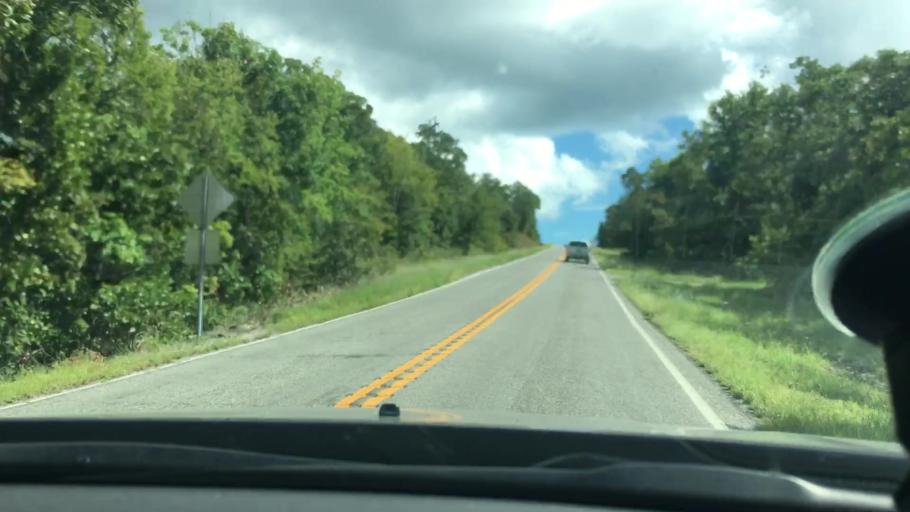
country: US
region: Oklahoma
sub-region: Sequoyah County
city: Vian
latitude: 35.6255
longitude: -94.9628
